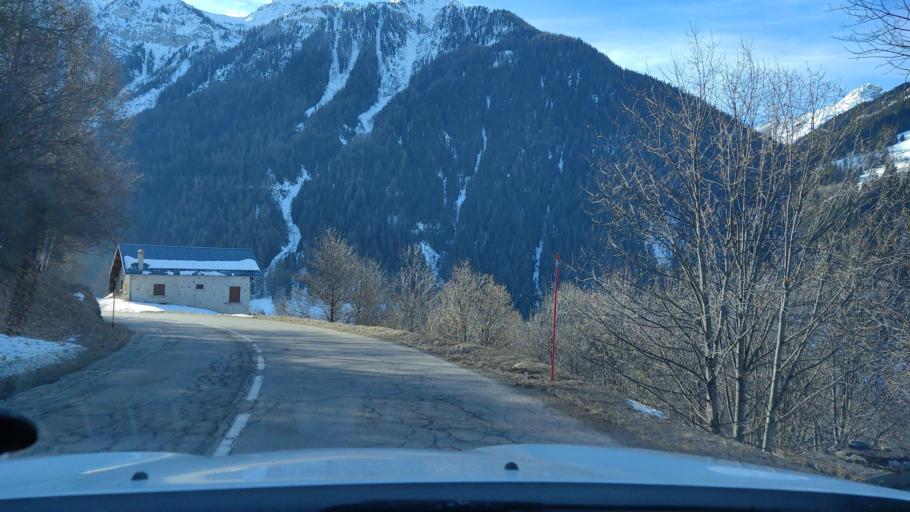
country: FR
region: Rhone-Alpes
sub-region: Departement de la Savoie
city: Belle-Plagne
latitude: 45.5441
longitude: 6.7605
